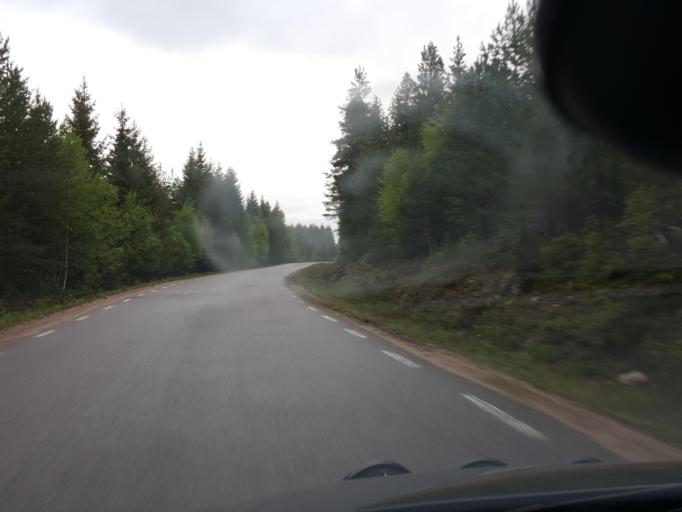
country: SE
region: Gaevleborg
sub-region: Ljusdals Kommun
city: Jaervsoe
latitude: 61.7432
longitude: 16.1900
